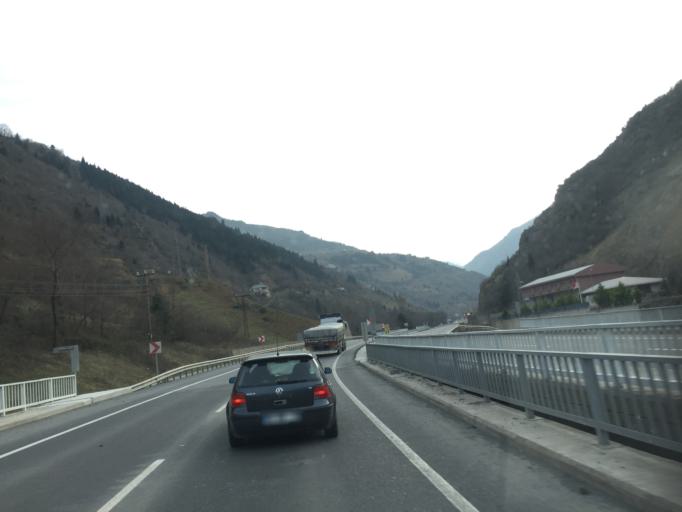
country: TR
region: Trabzon
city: Macka
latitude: 40.7973
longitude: 39.5845
